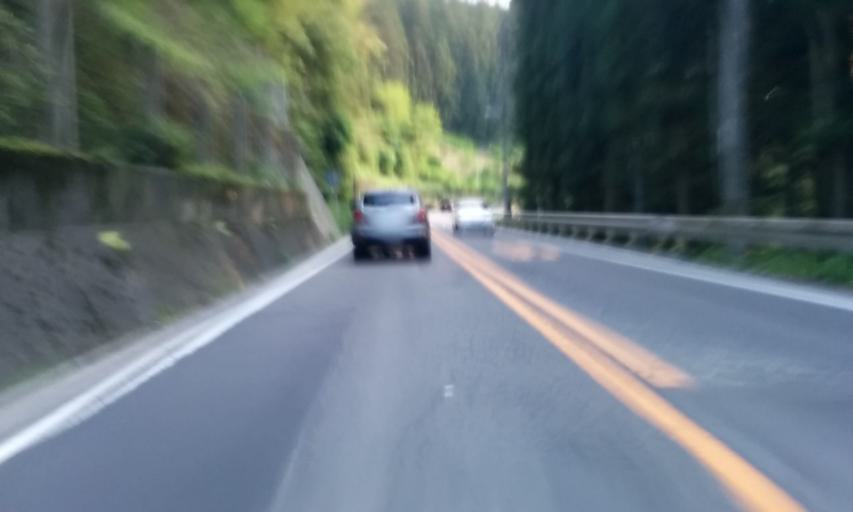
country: JP
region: Ehime
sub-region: Shikoku-chuo Shi
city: Matsuyama
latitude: 33.8234
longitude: 132.9827
